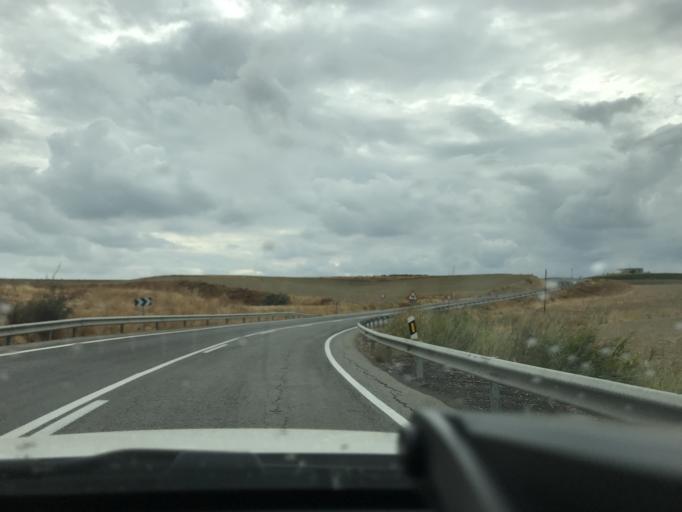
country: ES
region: Andalusia
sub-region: Provincia de Sevilla
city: Cantillana
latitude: 37.6175
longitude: -5.7948
